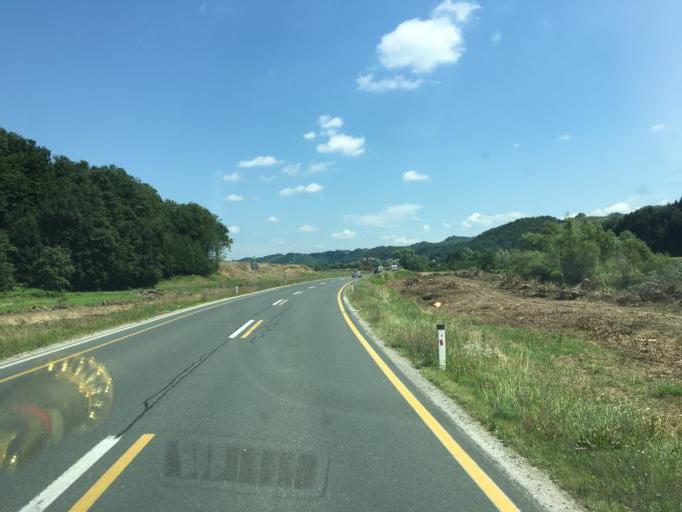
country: SI
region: Podlehnik
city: Podlehnik
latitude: 46.3069
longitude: 15.8622
